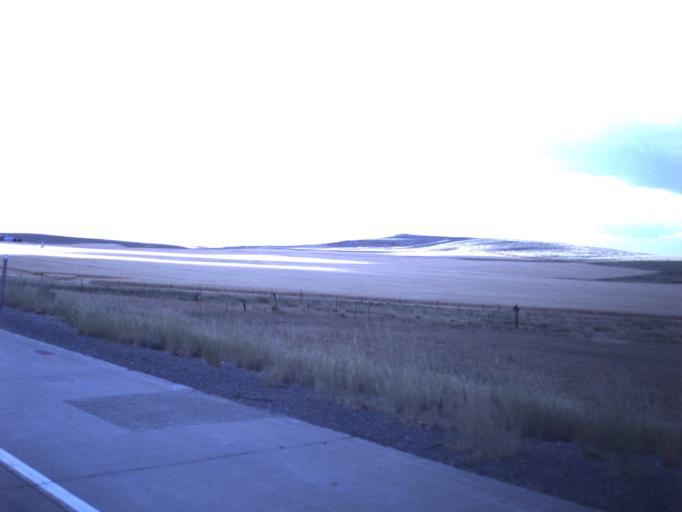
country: US
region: Utah
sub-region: Box Elder County
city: Garland
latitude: 41.8816
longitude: -112.4797
